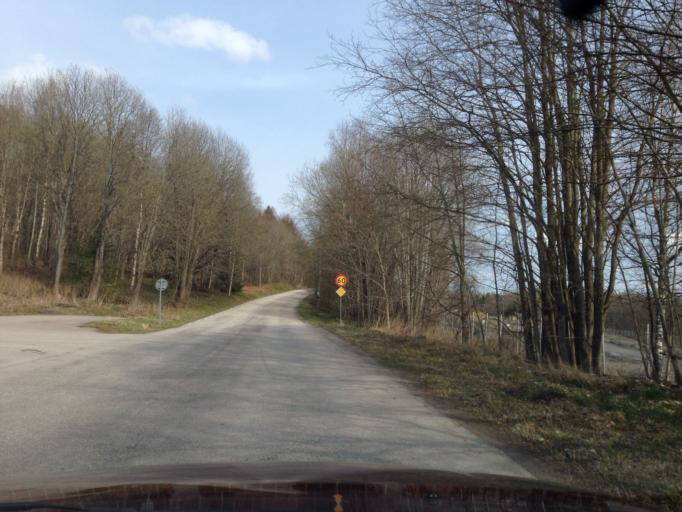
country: SE
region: Dalarna
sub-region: Ludvika Kommun
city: Grangesberg
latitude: 60.0812
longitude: 14.9904
